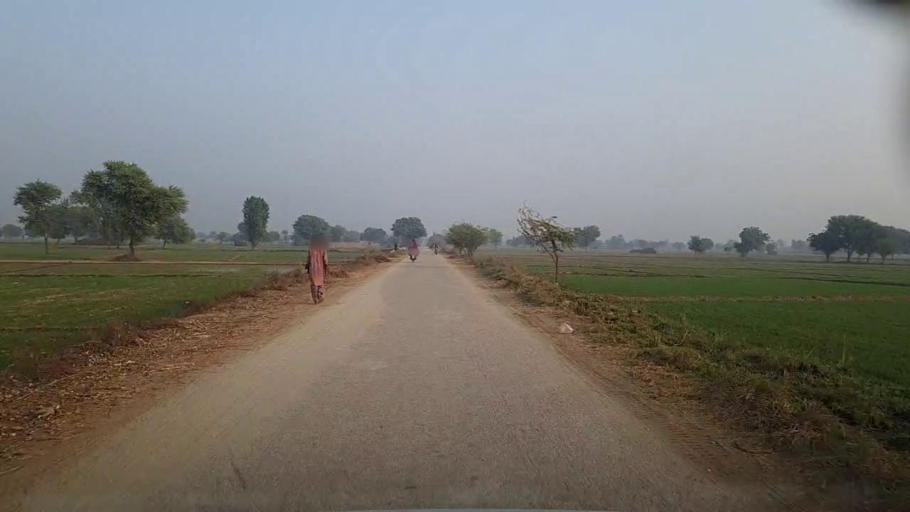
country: PK
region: Sindh
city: Bozdar
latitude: 27.0809
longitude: 68.5722
